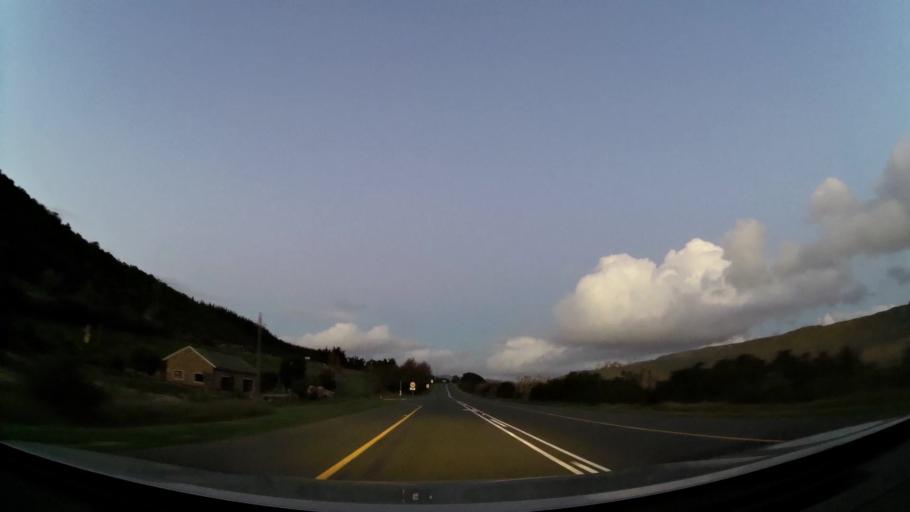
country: ZA
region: Western Cape
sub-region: Eden District Municipality
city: Knysna
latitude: -34.0228
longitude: 22.8449
